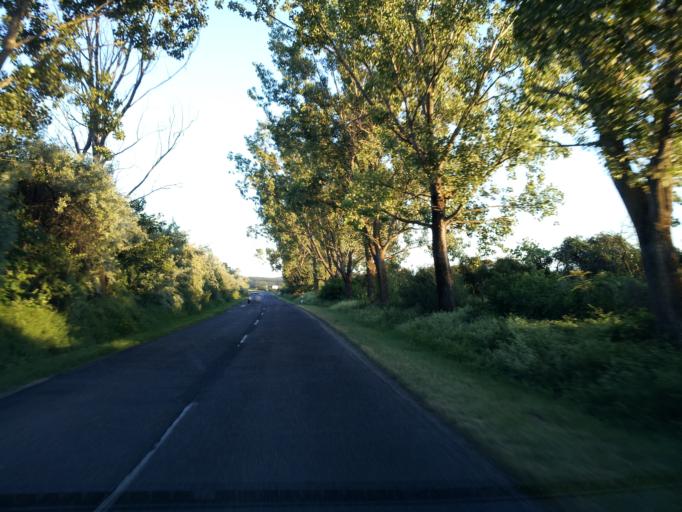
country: HU
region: Veszprem
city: Szentkiralyszabadja
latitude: 47.0415
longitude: 17.9308
